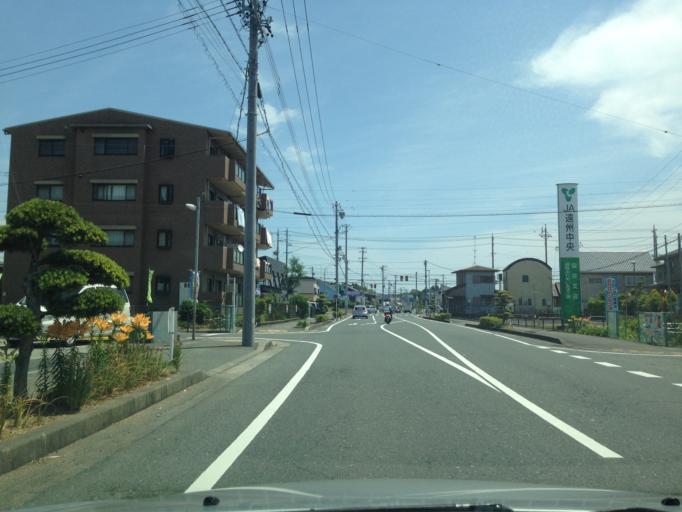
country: JP
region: Shizuoka
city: Fukuroi
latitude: 34.7588
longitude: 137.9169
